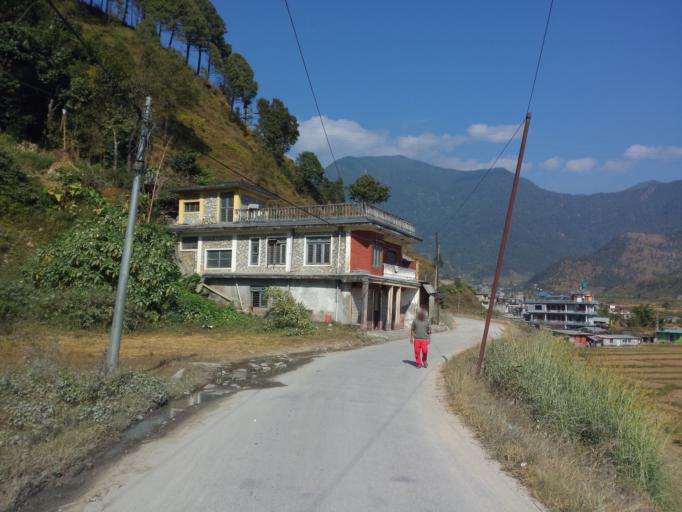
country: NP
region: Western Region
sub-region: Gandaki Zone
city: Pokhara
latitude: 28.2740
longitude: 83.9810
